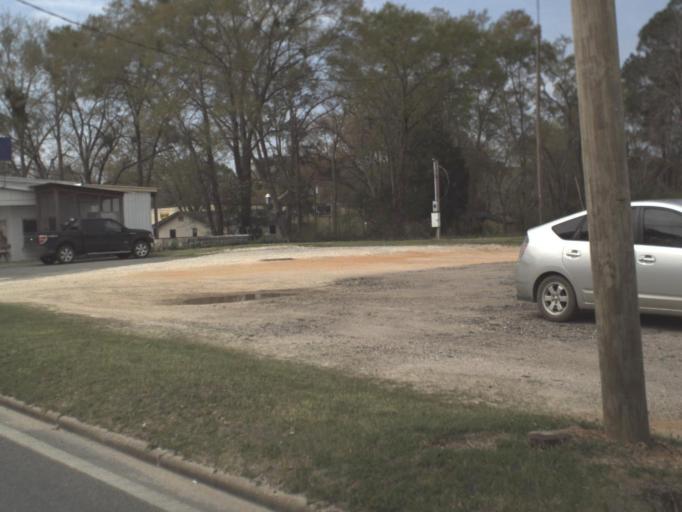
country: US
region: Florida
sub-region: Holmes County
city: Bonifay
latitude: 30.8021
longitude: -85.6790
